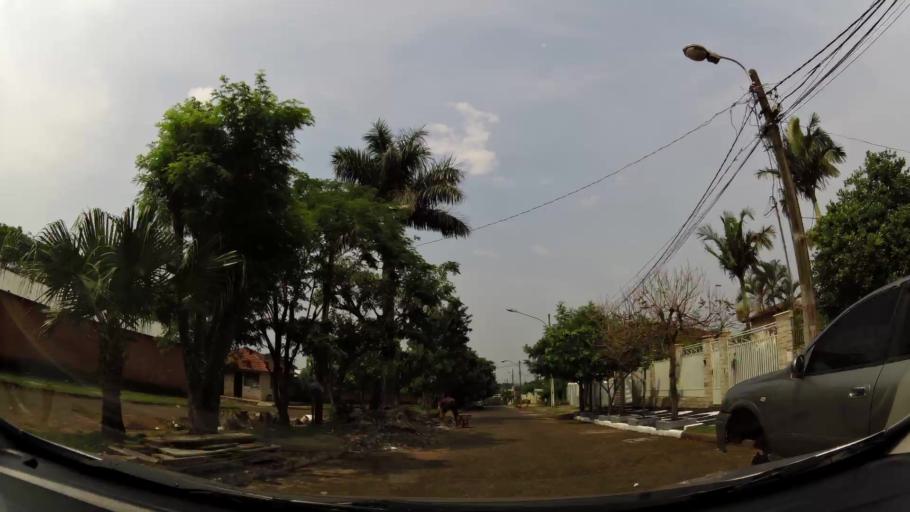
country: PY
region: Alto Parana
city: Presidente Franco
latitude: -25.5385
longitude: -54.6289
